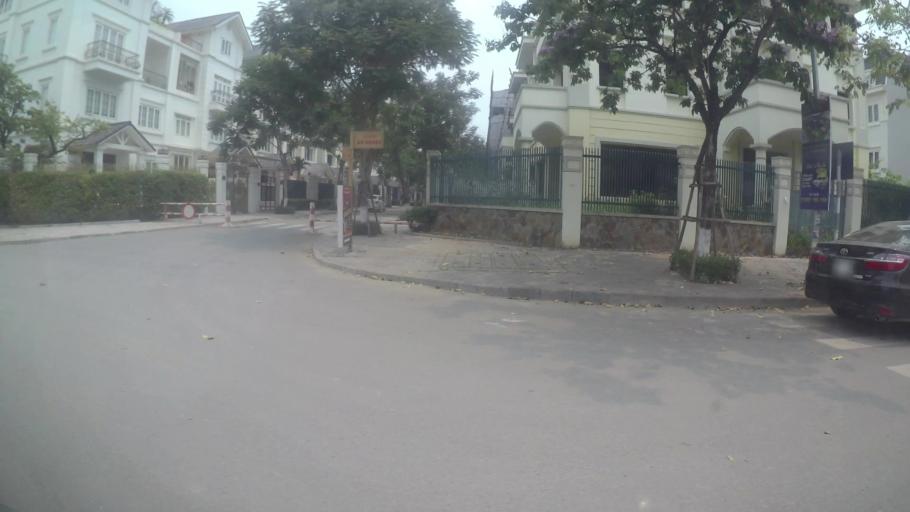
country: VN
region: Ha Noi
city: Ha Dong
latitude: 20.9779
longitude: 105.7593
